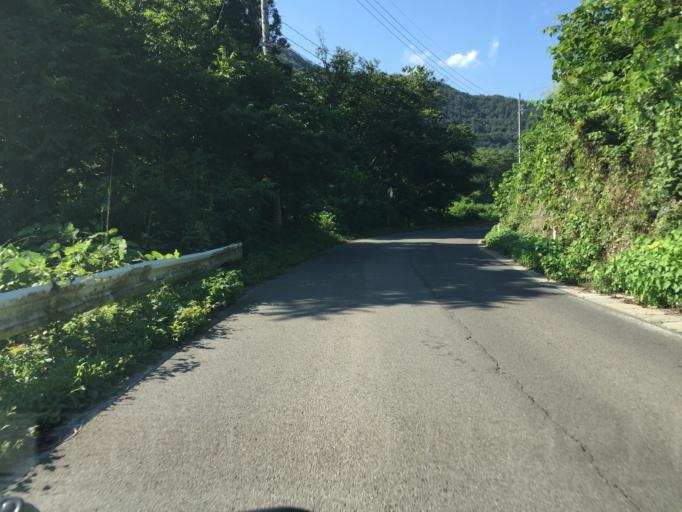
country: JP
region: Fukushima
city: Fukushima-shi
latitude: 37.8753
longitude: 140.4324
